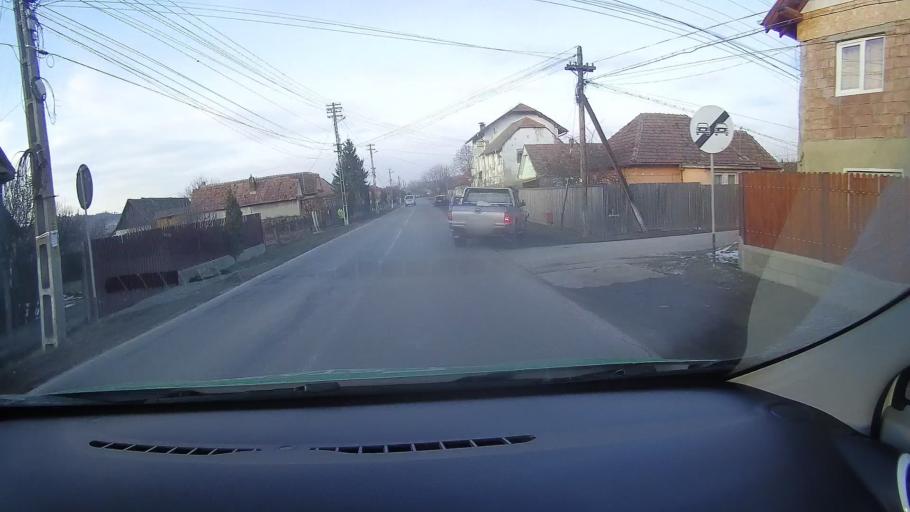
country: RO
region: Mures
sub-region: Comuna Vanatori
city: Vanatori
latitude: 46.2438
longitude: 24.9233
